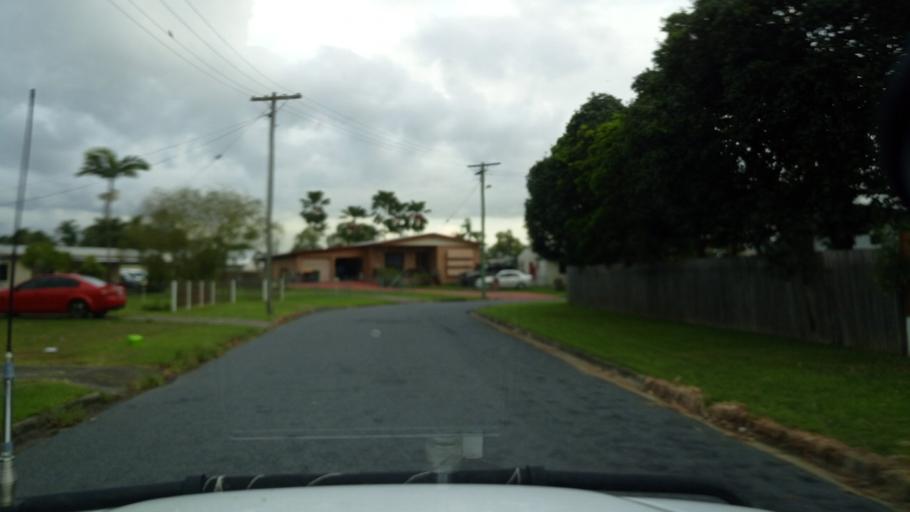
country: AU
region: Queensland
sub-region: Cairns
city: Woree
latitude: -16.9305
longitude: 145.7395
